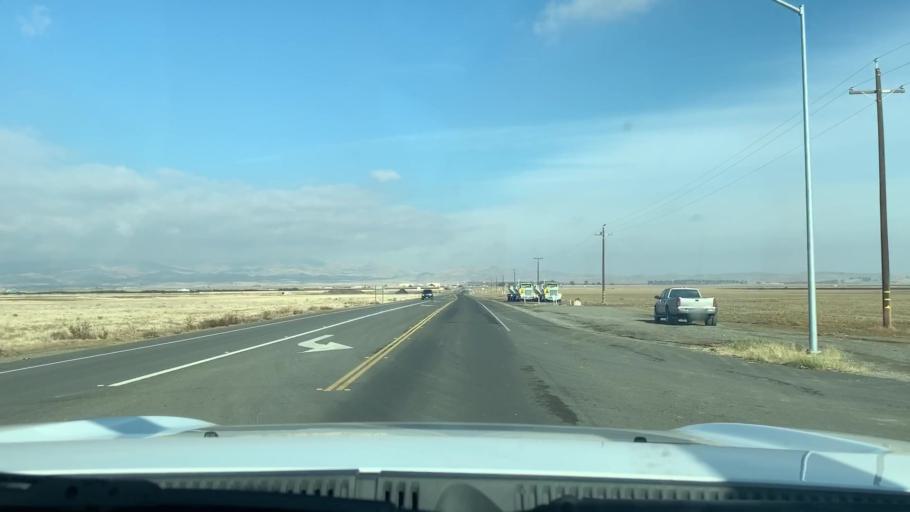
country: US
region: California
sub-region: Fresno County
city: Coalinga
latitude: 36.1569
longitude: -120.3544
